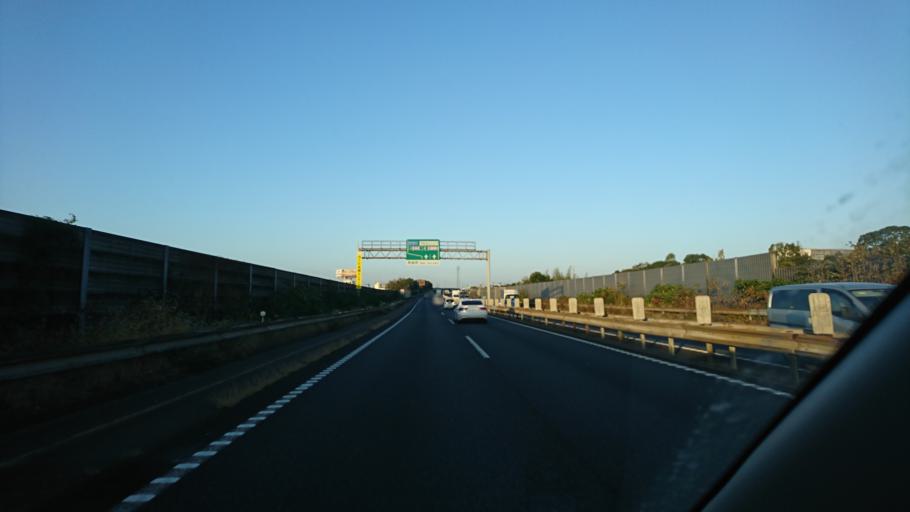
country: JP
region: Hyogo
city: Kakogawacho-honmachi
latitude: 34.7165
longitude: 134.9096
